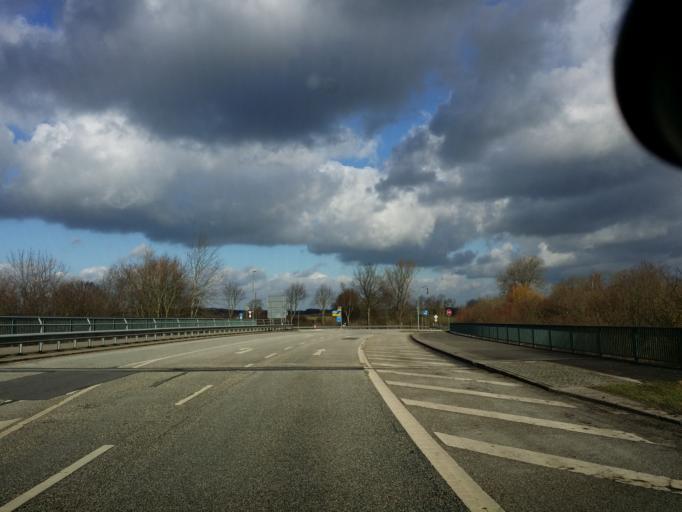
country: DE
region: Schleswig-Holstein
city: Bredenbek
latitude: 54.3172
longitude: 9.8540
